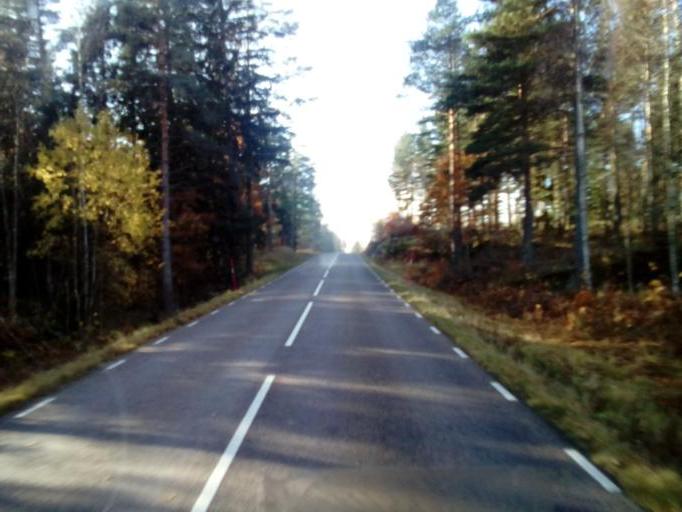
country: SE
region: Kalmar
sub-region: Vasterviks Kommun
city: Ankarsrum
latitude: 57.7745
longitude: 16.1518
